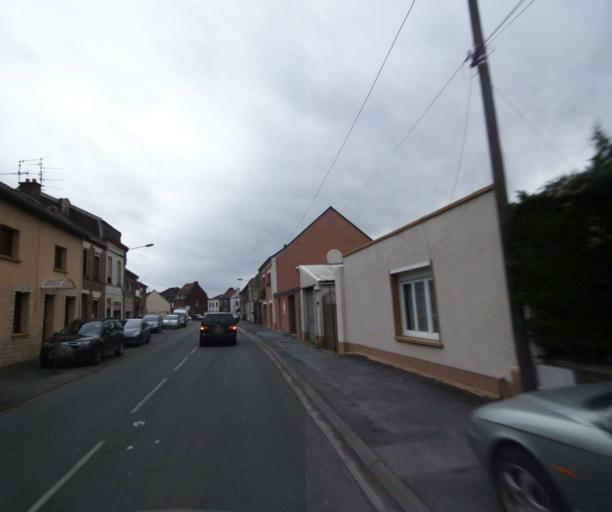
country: FR
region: Nord-Pas-de-Calais
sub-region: Departement du Nord
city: Anzin
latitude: 50.3804
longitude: 3.5122
